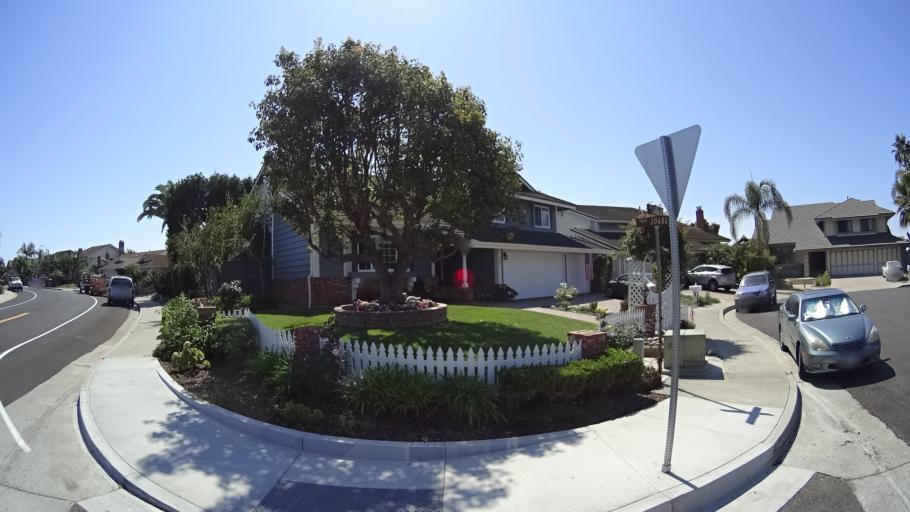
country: US
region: California
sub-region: Orange County
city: San Clemente
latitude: 33.4529
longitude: -117.6414
